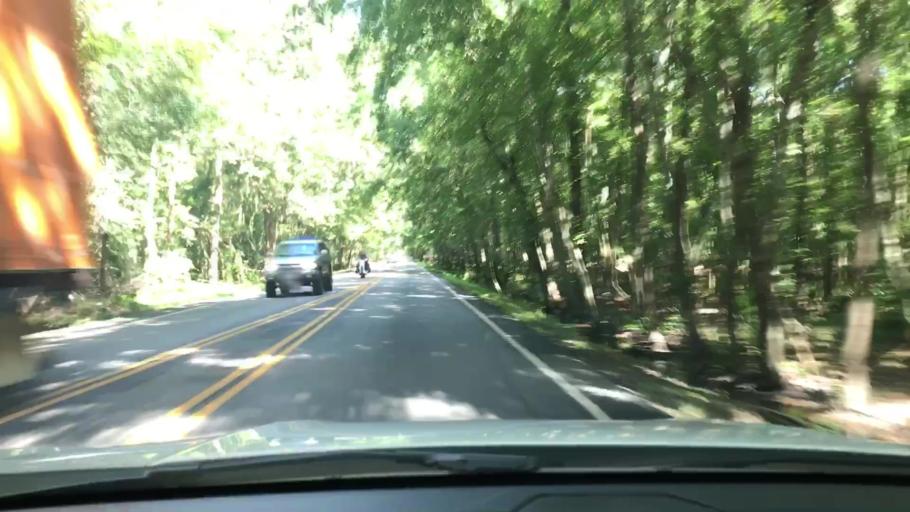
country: US
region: South Carolina
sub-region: Charleston County
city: Shell Point
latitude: 32.8598
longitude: -80.0772
